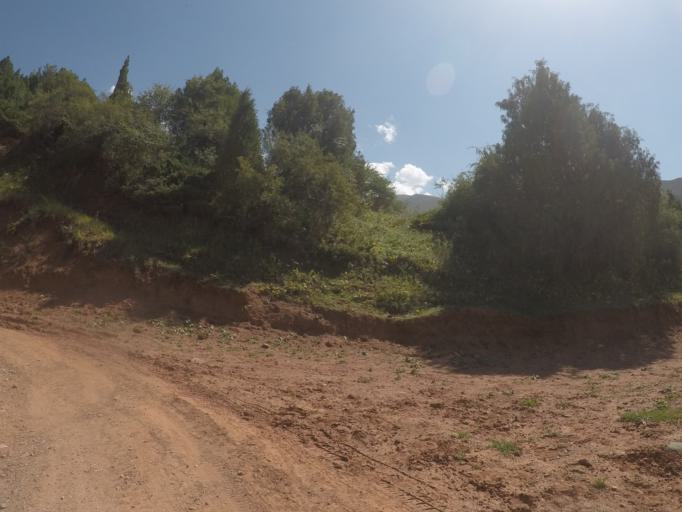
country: KG
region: Chuy
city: Bishkek
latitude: 42.6470
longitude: 74.5774
